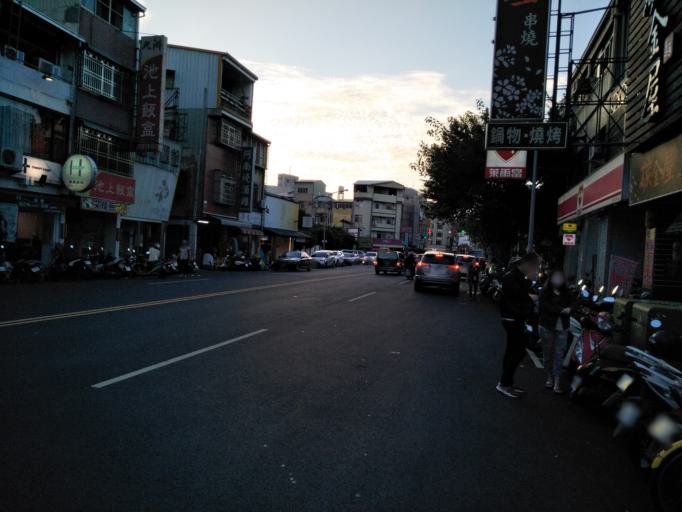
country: TW
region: Taiwan
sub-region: Taichung City
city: Taichung
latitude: 24.1486
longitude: 120.6827
